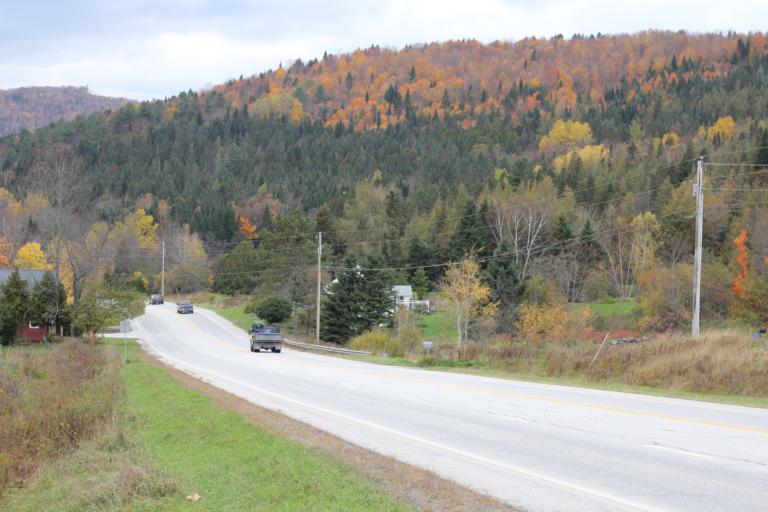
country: US
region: Vermont
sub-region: Caledonia County
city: Hardwick
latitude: 44.3903
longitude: -72.2483
